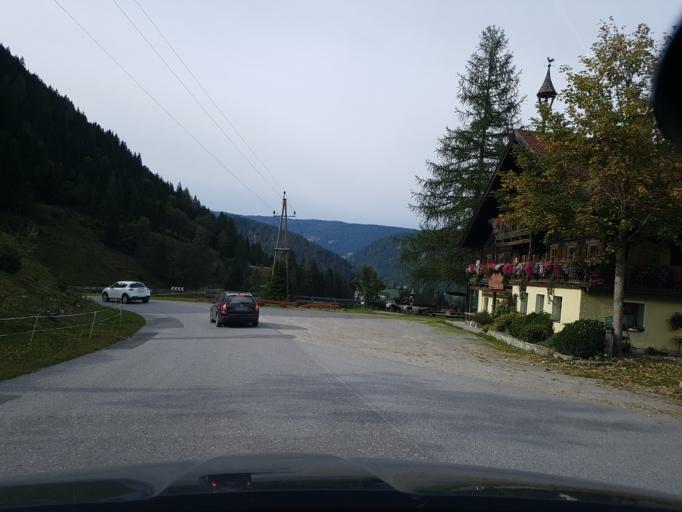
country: AT
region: Salzburg
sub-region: Politischer Bezirk Sankt Johann im Pongau
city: Forstau
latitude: 47.3654
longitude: 13.5565
